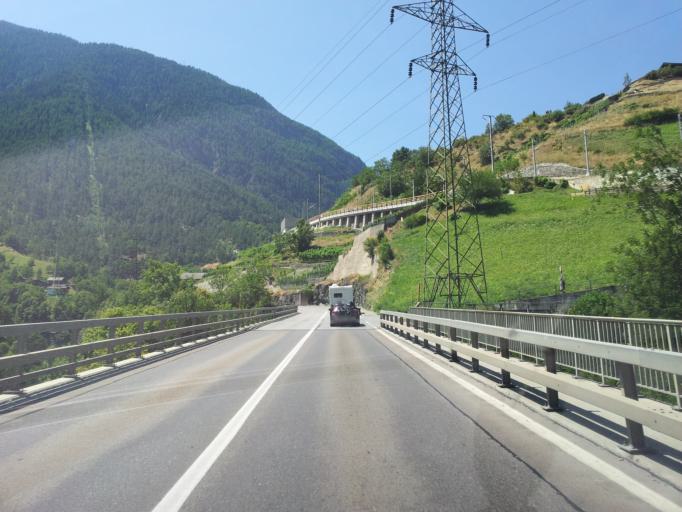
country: CH
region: Valais
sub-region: Visp District
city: Stalden
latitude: 46.2341
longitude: 7.8736
